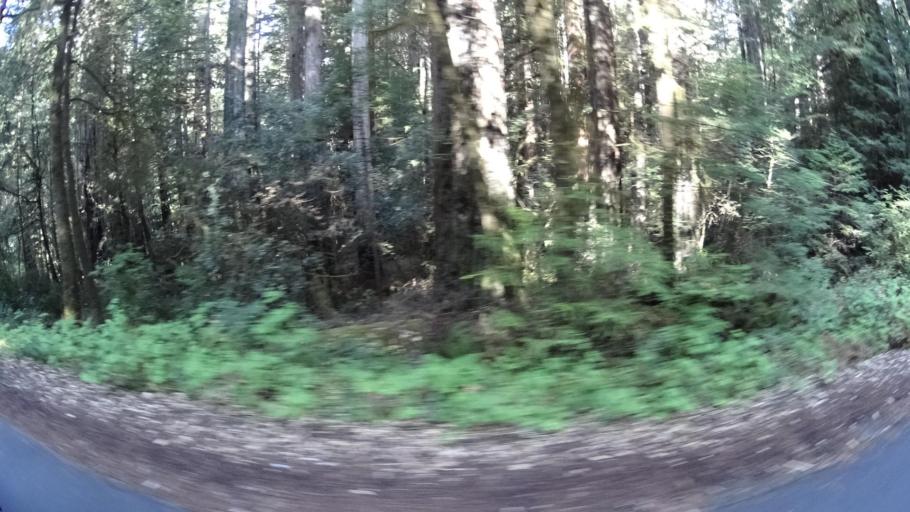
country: US
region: California
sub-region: Humboldt County
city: Rio Dell
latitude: 40.3460
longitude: -123.9535
